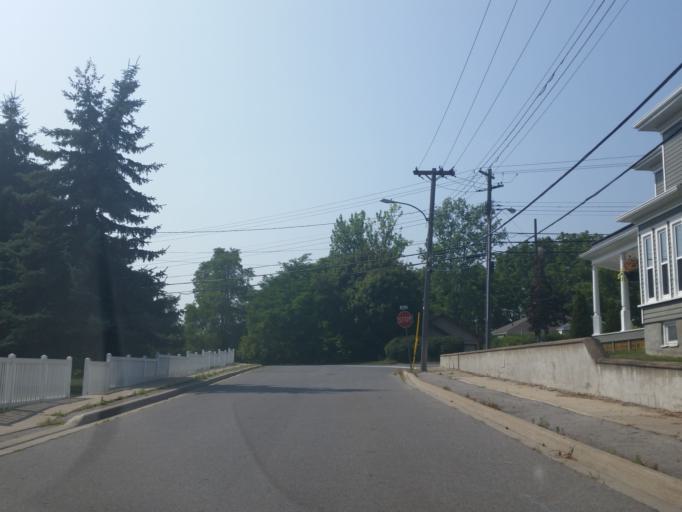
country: CA
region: Ontario
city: Picton
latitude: 44.0105
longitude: -77.1313
